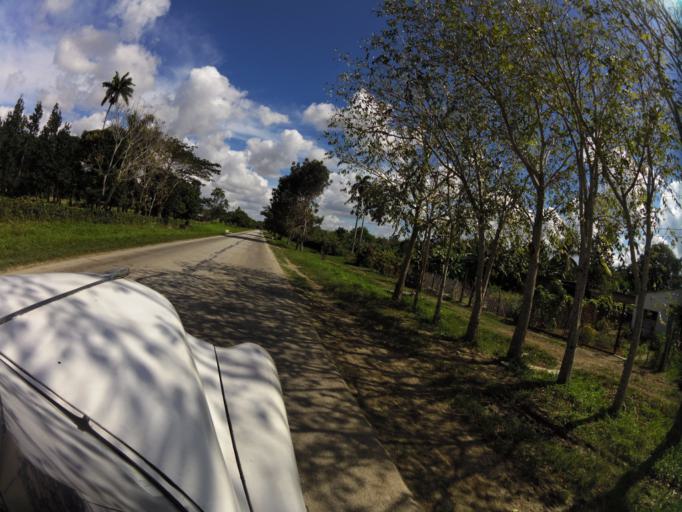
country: CU
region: Holguin
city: Cacocum
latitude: 20.8590
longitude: -76.4542
